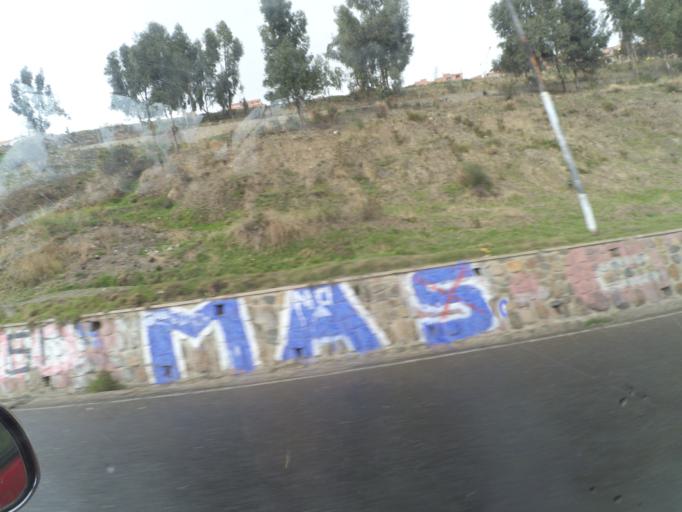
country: BO
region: La Paz
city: La Paz
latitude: -16.4945
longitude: -68.1663
